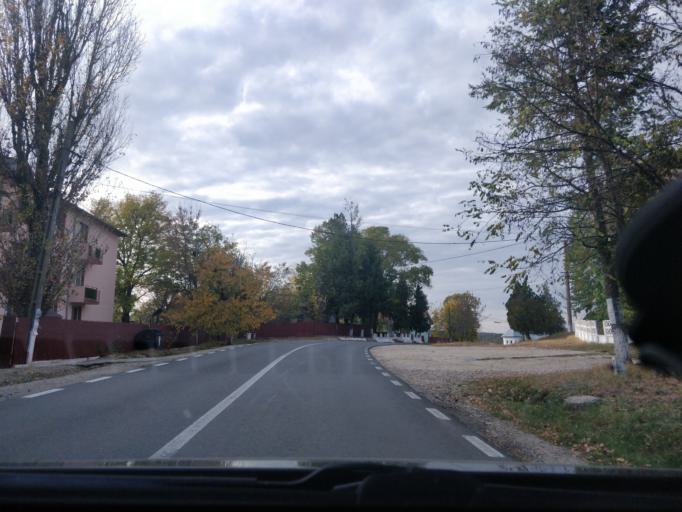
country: RO
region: Giurgiu
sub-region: Comuna Bucsani
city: Bucsani
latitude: 44.3678
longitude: 25.6613
